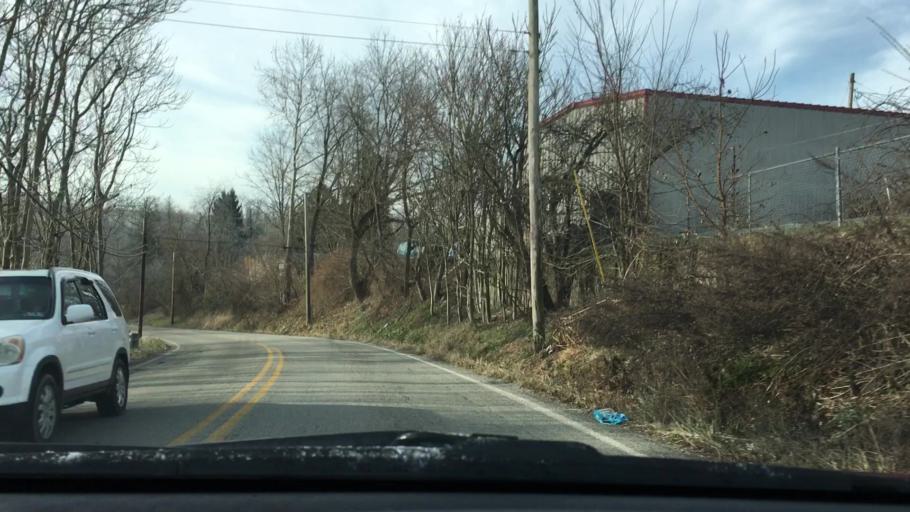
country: US
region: Pennsylvania
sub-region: Westmoreland County
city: Irwin
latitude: 40.2633
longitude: -79.7035
